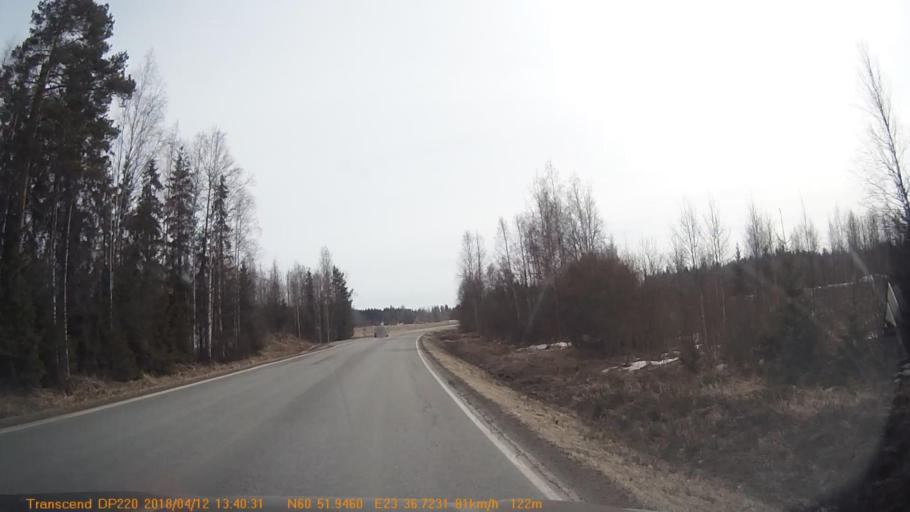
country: FI
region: Haeme
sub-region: Forssa
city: Forssa
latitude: 60.8652
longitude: 23.6127
